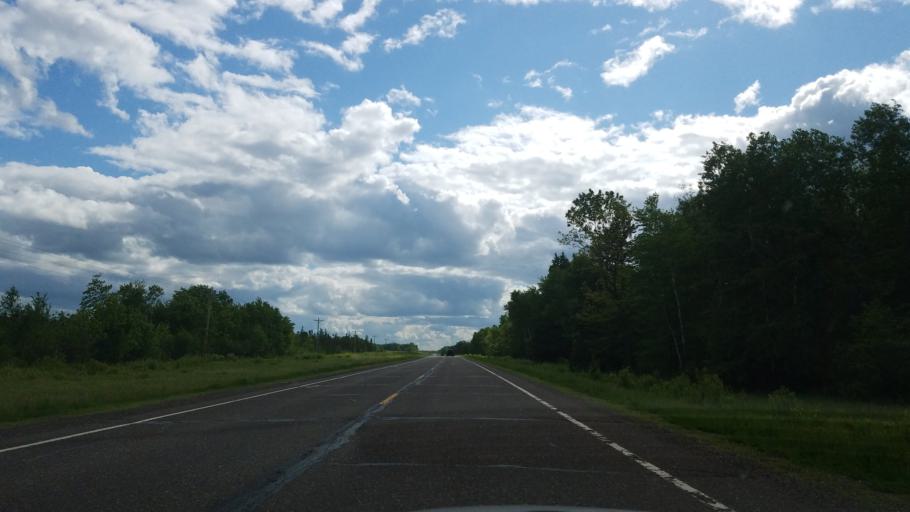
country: US
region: Wisconsin
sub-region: Burnett County
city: Siren
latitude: 46.1908
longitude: -92.1795
